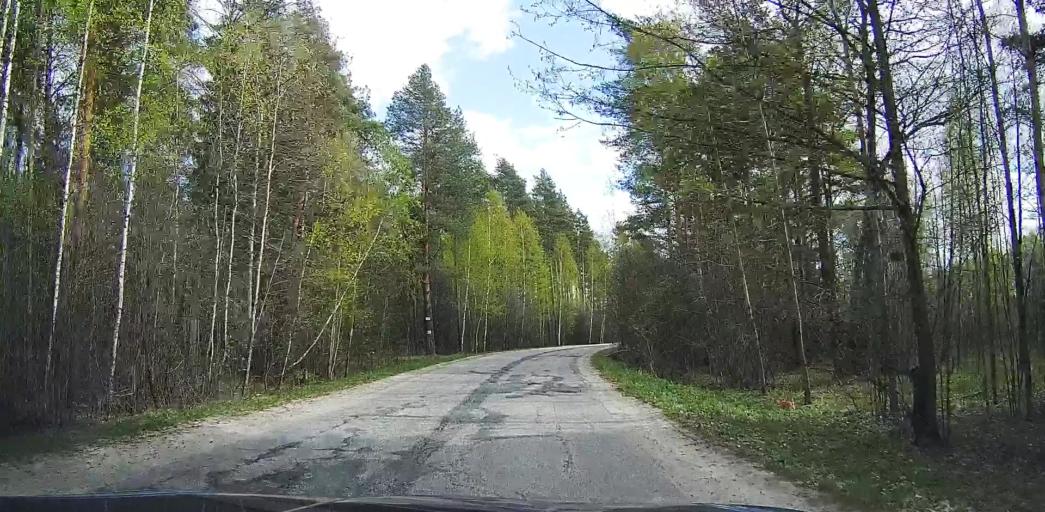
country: RU
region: Moskovskaya
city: Davydovo
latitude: 55.6444
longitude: 38.7729
